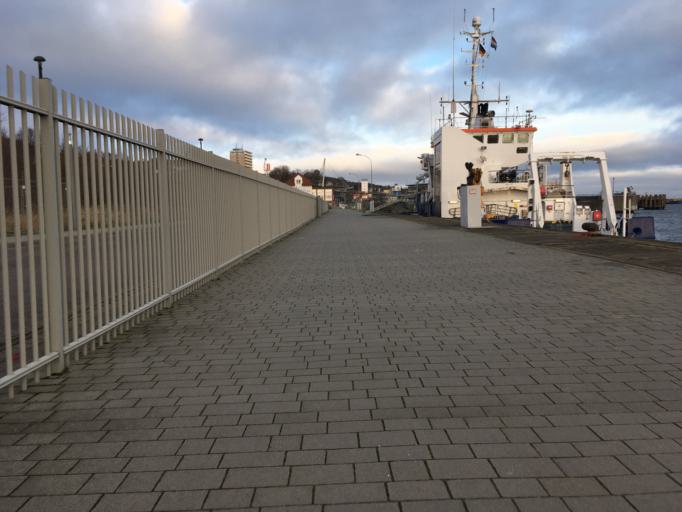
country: DE
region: Mecklenburg-Vorpommern
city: Sassnitz
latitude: 54.5100
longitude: 13.6357
